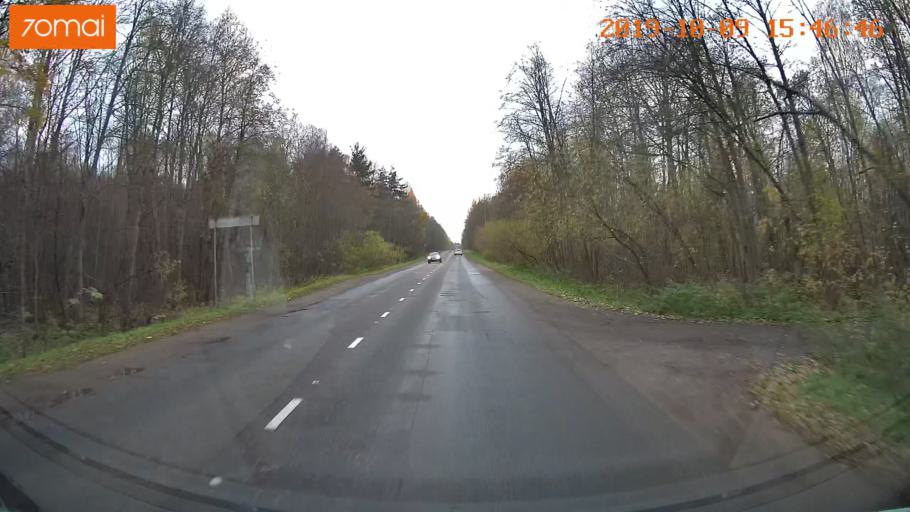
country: RU
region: Kostroma
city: Oktyabr'skiy
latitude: 57.8222
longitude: 41.0387
